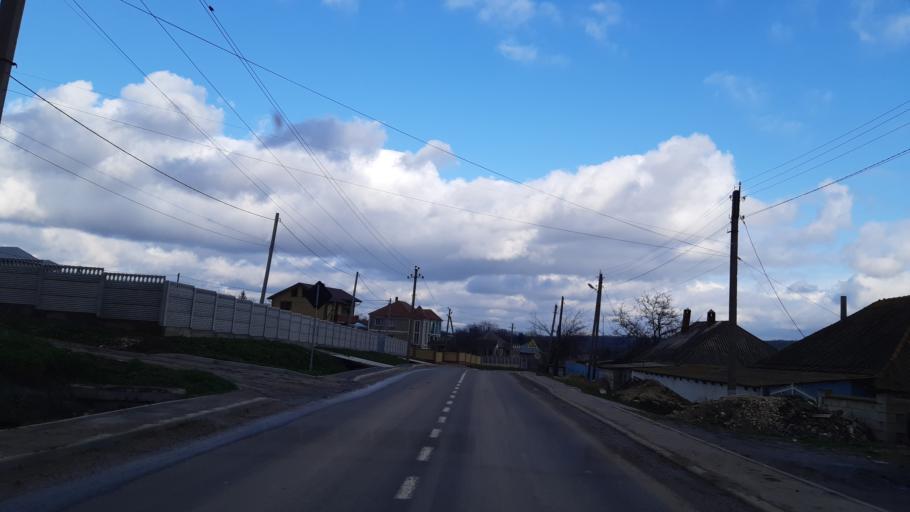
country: MD
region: Telenesti
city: Cocieri
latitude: 47.2228
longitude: 29.0111
